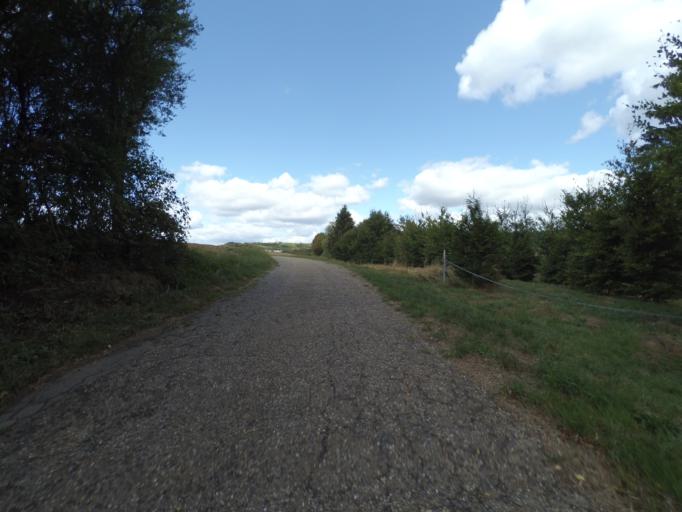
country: LU
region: Grevenmacher
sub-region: Canton de Remich
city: Lenningen
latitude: 49.6135
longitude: 6.3670
